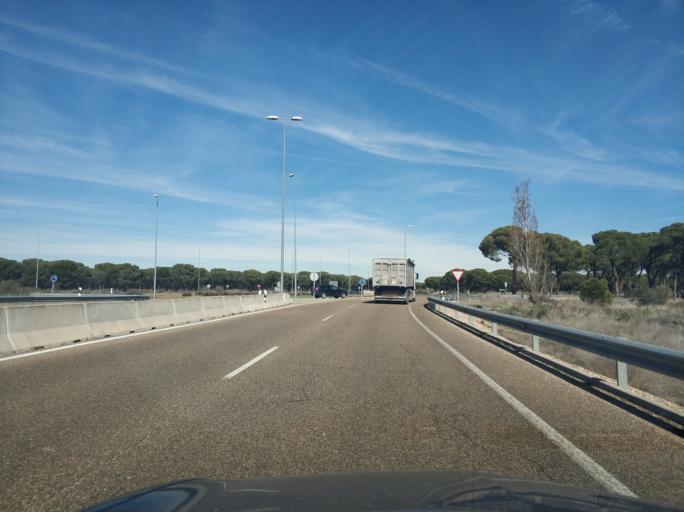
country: ES
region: Castille and Leon
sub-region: Provincia de Valladolid
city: Viana de Cega
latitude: 41.5611
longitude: -4.7867
